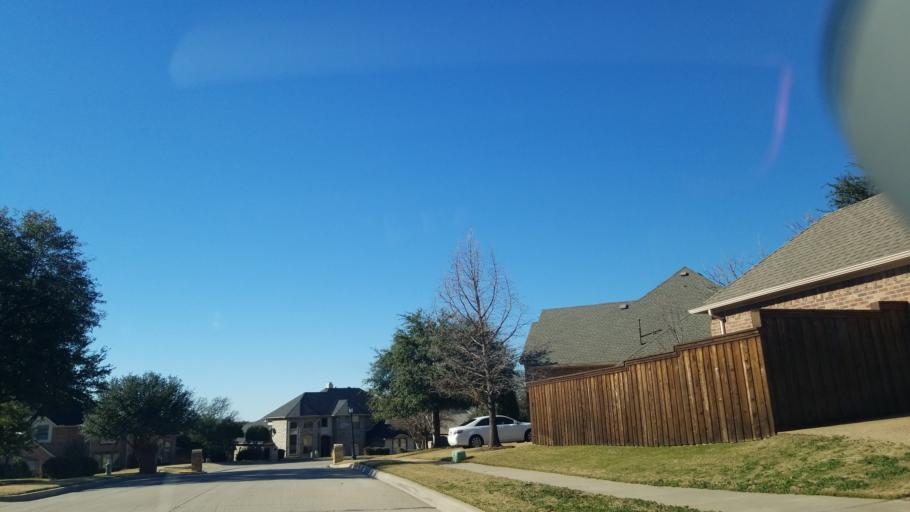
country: US
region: Texas
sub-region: Denton County
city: Corinth
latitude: 33.1524
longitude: -97.0873
